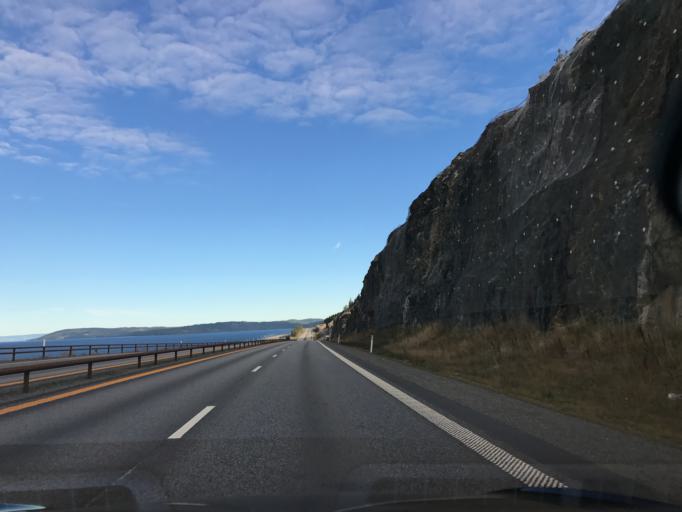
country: NO
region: Akershus
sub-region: Eidsvoll
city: Eidsvoll
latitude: 60.5217
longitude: 11.2423
